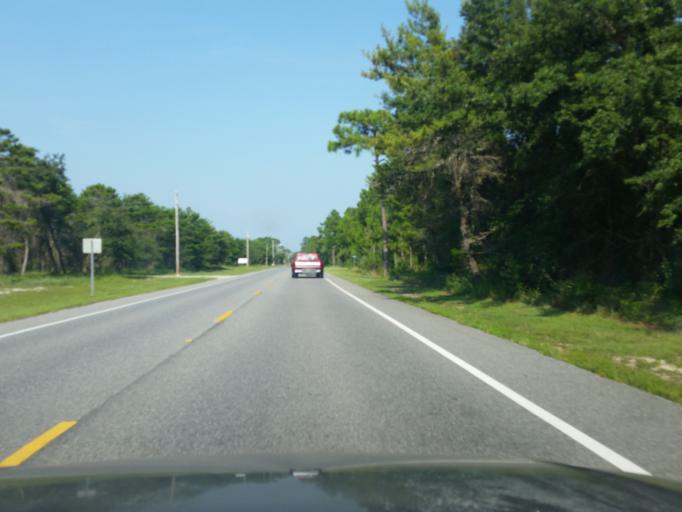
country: US
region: Alabama
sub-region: Baldwin County
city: Gulf Shores
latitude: 30.2539
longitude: -87.7373
